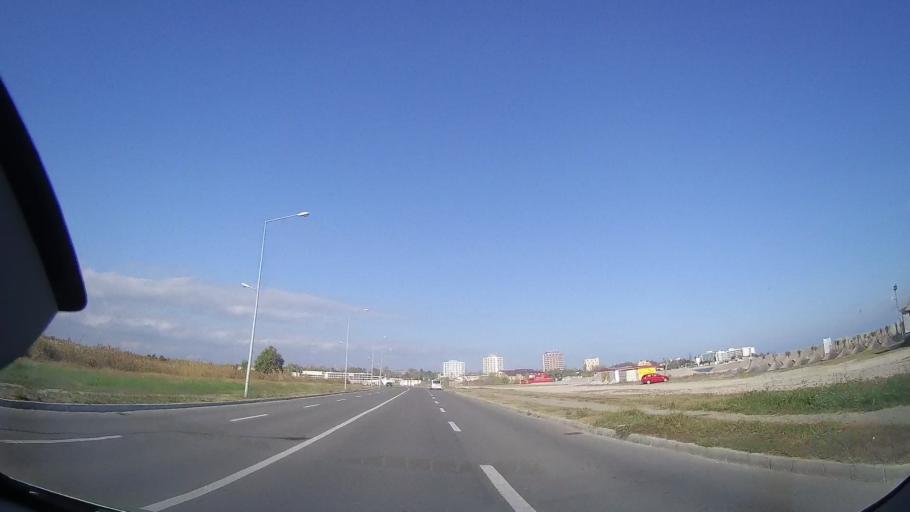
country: RO
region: Constanta
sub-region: Municipiul Mangalia
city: Mangalia
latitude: 43.8385
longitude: 28.5898
